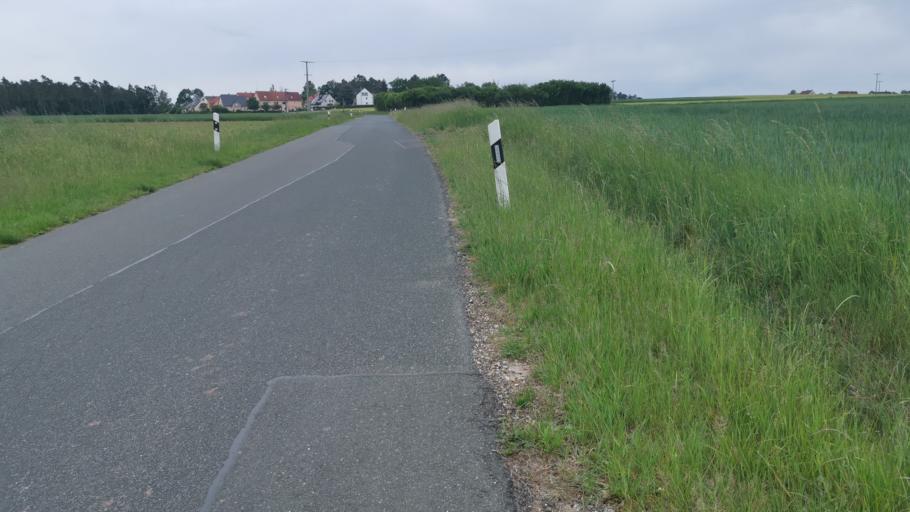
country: DE
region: Bavaria
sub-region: Regierungsbezirk Mittelfranken
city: Schwabach
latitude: 49.3711
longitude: 11.0150
